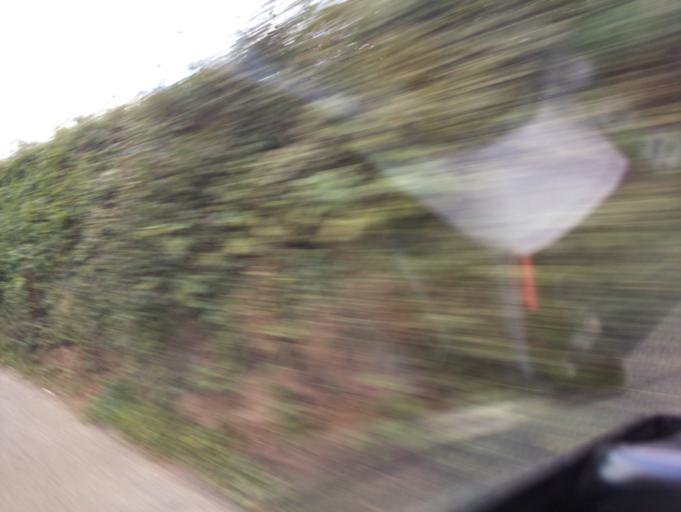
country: GB
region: England
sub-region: Devon
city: Sidmouth
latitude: 50.7284
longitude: -3.2161
